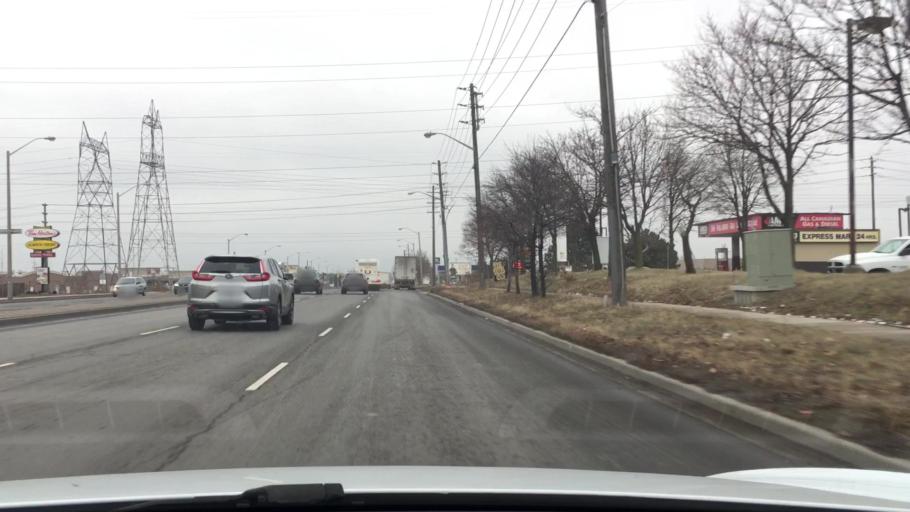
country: CA
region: Ontario
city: Markham
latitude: 43.8236
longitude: -79.2478
